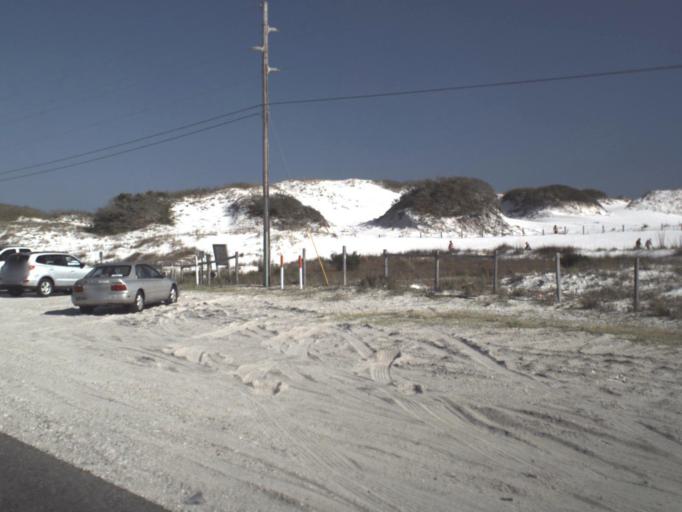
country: US
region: Florida
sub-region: Okaloosa County
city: Destin
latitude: 30.3921
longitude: -86.5469
